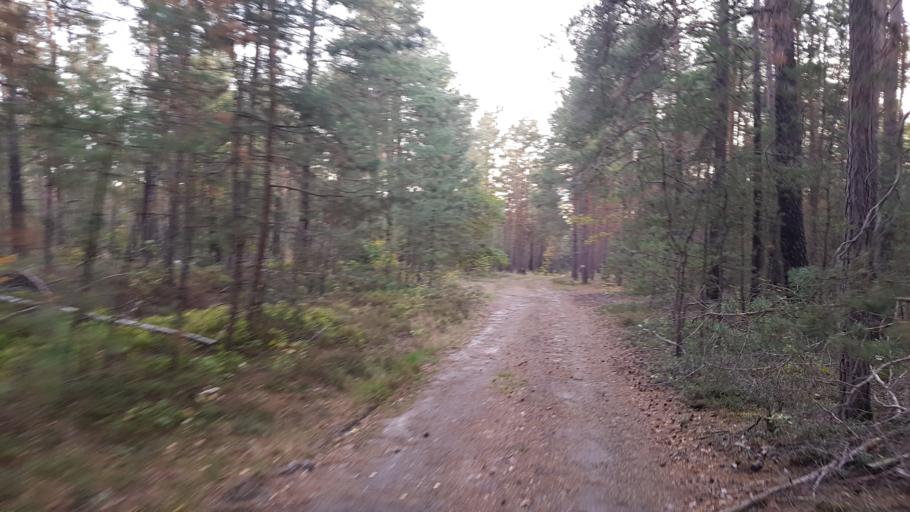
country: DE
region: Brandenburg
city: Trobitz
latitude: 51.5544
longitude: 13.4367
